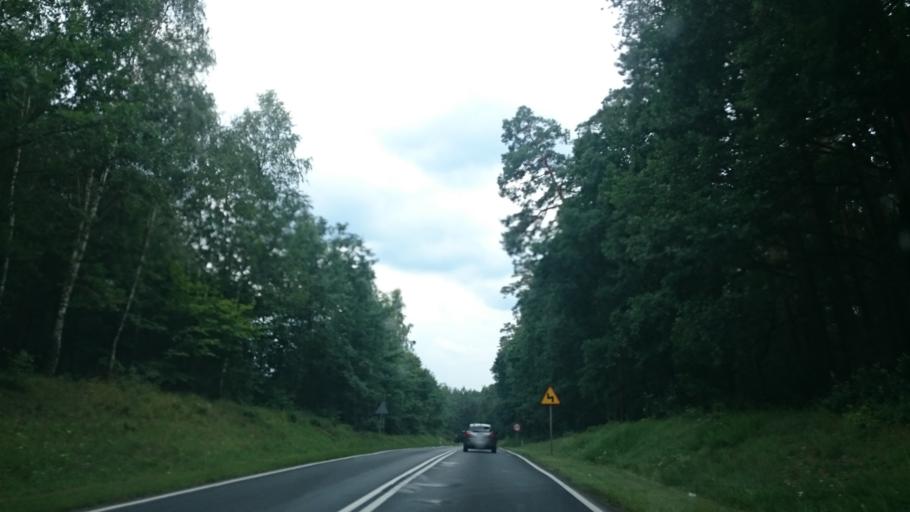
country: PL
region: Kujawsko-Pomorskie
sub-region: Powiat tucholski
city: Tuchola
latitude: 53.5582
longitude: 17.9014
